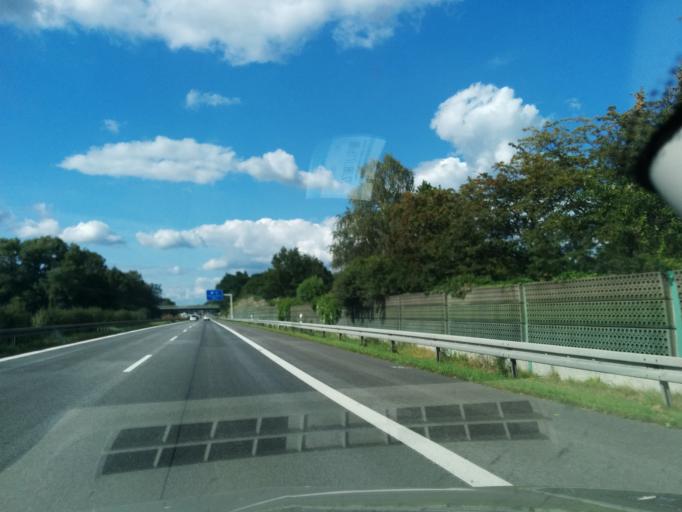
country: DE
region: Brandenburg
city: Bernau bei Berlin
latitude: 52.6788
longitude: 13.5643
